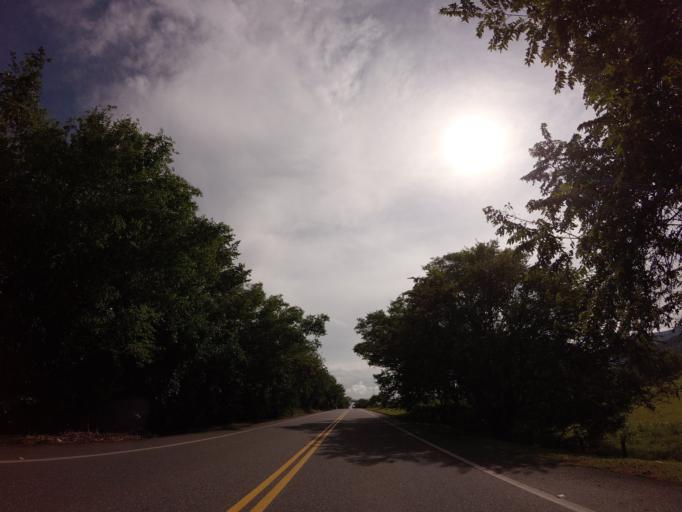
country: CO
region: Tolima
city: Honda
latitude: 5.3001
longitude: -74.7430
